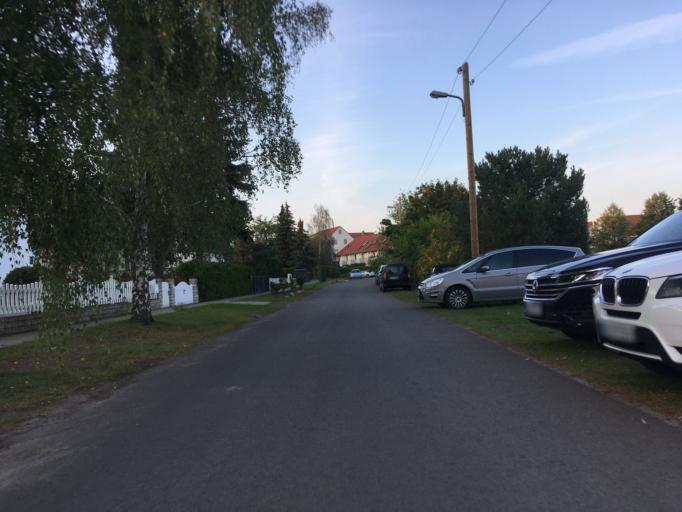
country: DE
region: Berlin
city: Biesdorf
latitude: 52.4973
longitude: 13.5486
